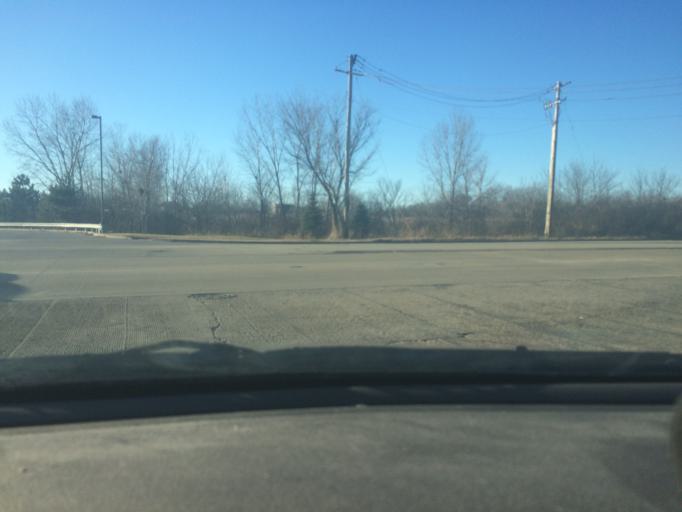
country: US
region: Illinois
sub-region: Cook County
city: Streamwood
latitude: 42.0222
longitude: -88.2027
